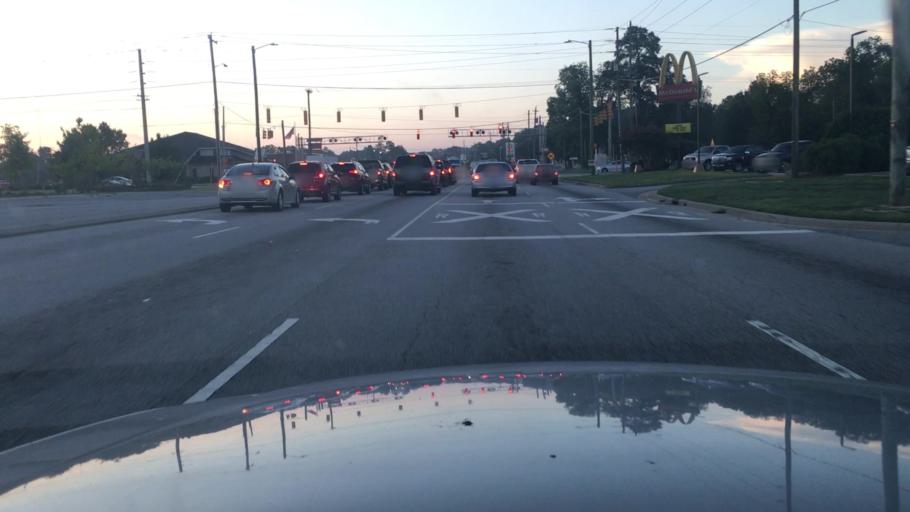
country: US
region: North Carolina
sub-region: Cumberland County
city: Fort Bragg
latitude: 35.0618
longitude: -79.0163
